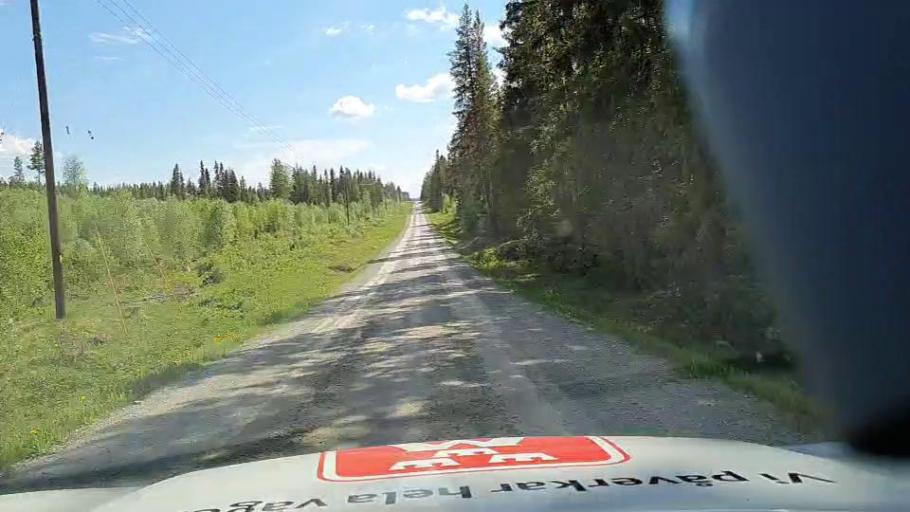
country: SE
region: Jaemtland
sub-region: Stroemsunds Kommun
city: Stroemsund
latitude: 64.4850
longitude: 15.5917
